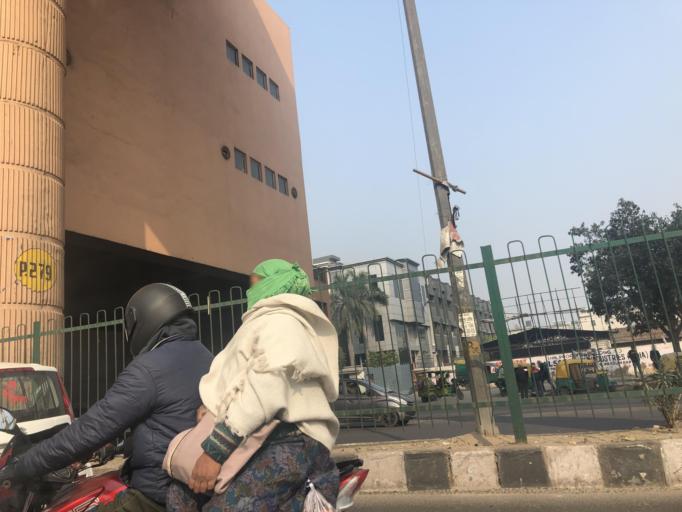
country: IN
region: NCT
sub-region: West Delhi
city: Nangloi Jat
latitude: 28.6796
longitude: 77.0933
